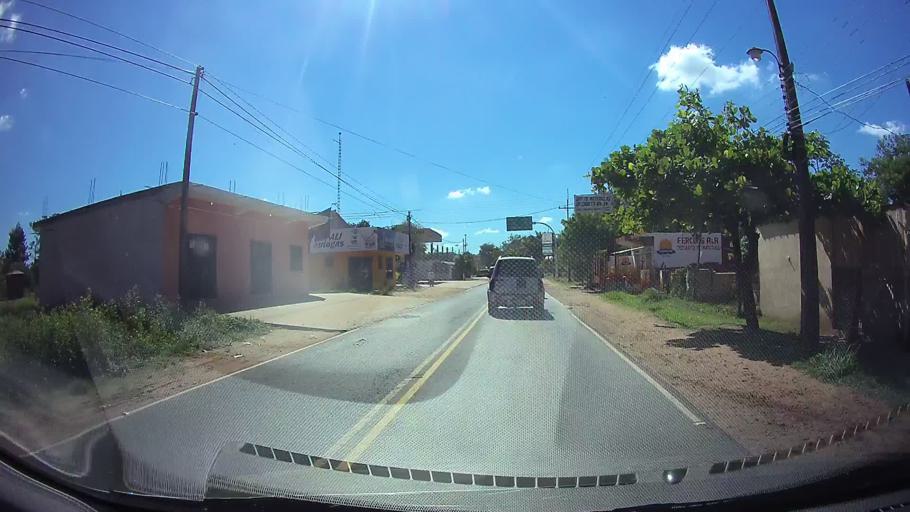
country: PY
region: Central
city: Limpio
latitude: -25.1932
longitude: -57.4634
